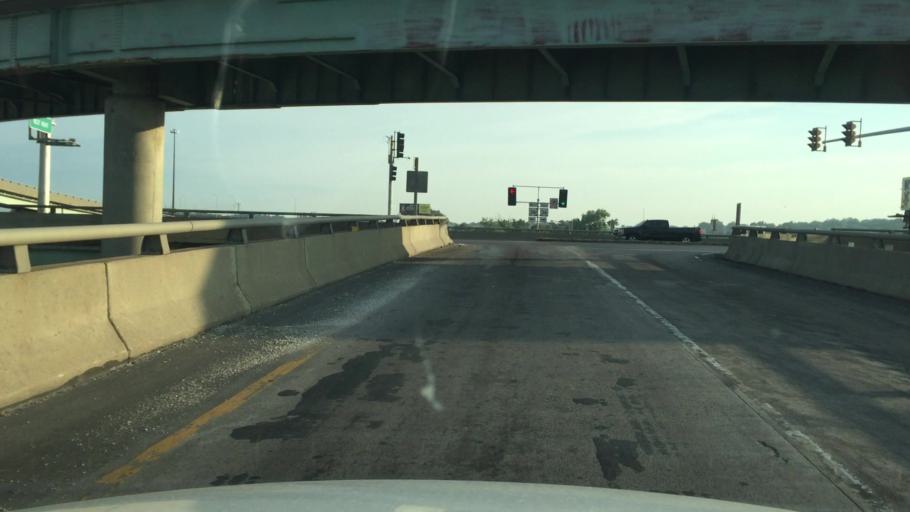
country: US
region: Kansas
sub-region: Doniphan County
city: Elwood
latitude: 39.7483
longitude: -94.8532
